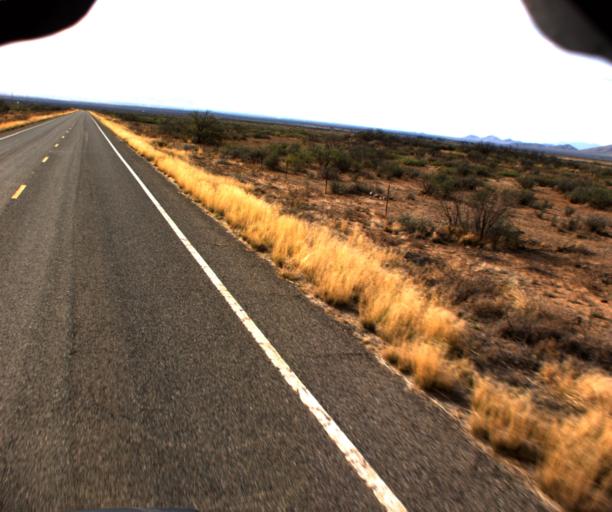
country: US
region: Arizona
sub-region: Cochise County
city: Willcox
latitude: 32.1926
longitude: -109.7001
